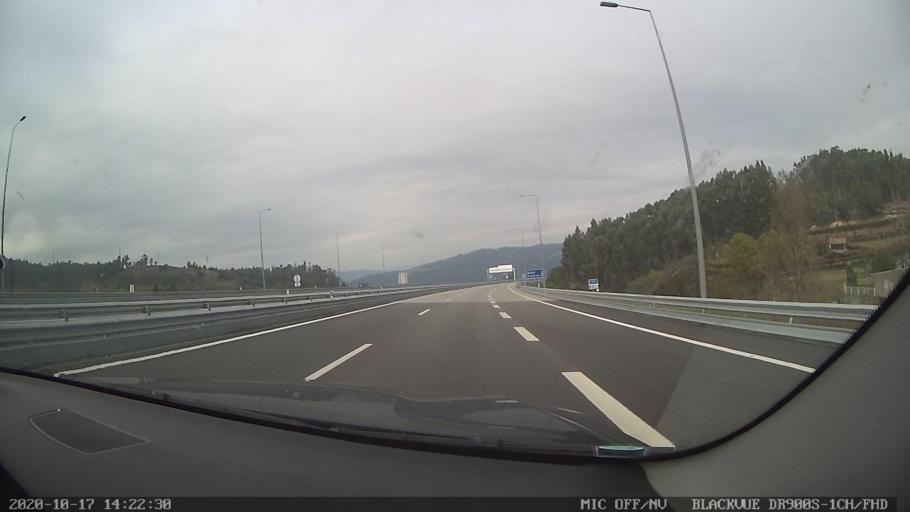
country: PT
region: Porto
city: Barrosas
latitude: 41.3515
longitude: -8.2667
